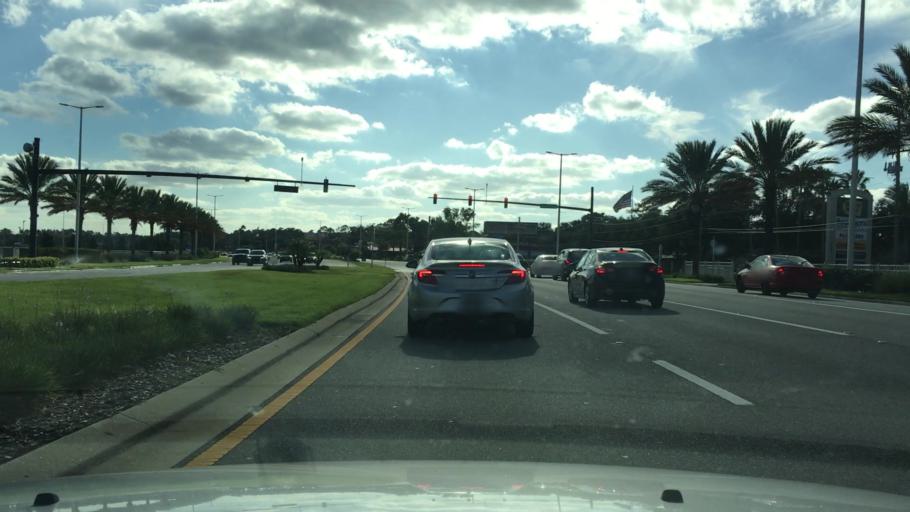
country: US
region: Florida
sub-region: Volusia County
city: Daytona Beach
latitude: 29.1903
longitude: -81.0712
